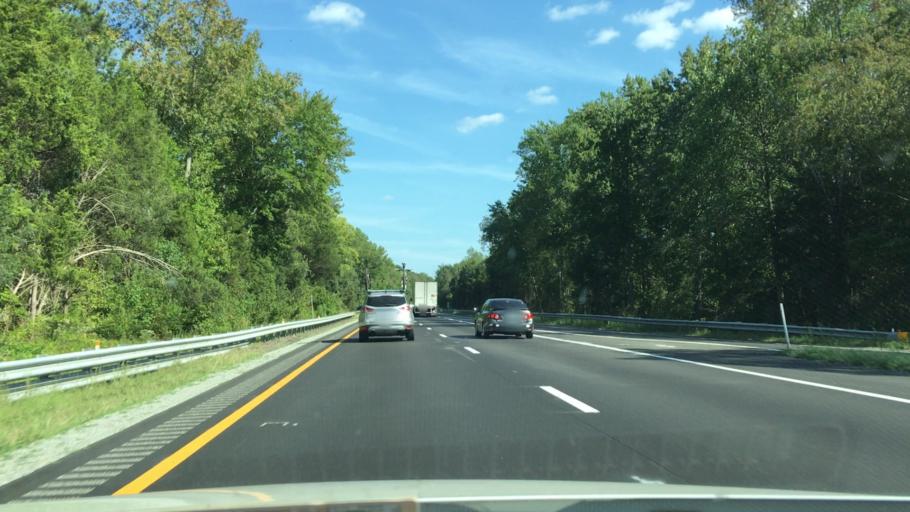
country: US
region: Virginia
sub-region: Goochland County
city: Goochland
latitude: 37.7098
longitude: -77.7807
